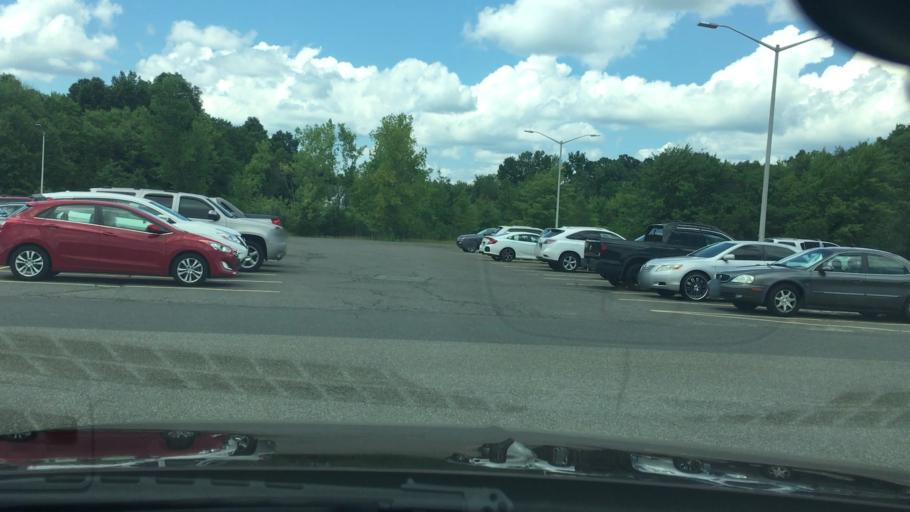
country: US
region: Connecticut
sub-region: Hartford County
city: Kensington
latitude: 41.6461
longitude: -72.7426
